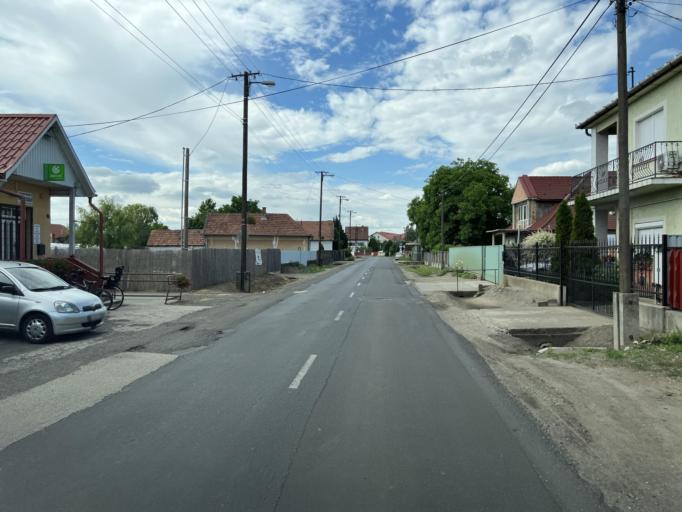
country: HU
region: Pest
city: Szentlorinckata
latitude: 47.5212
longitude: 19.7545
